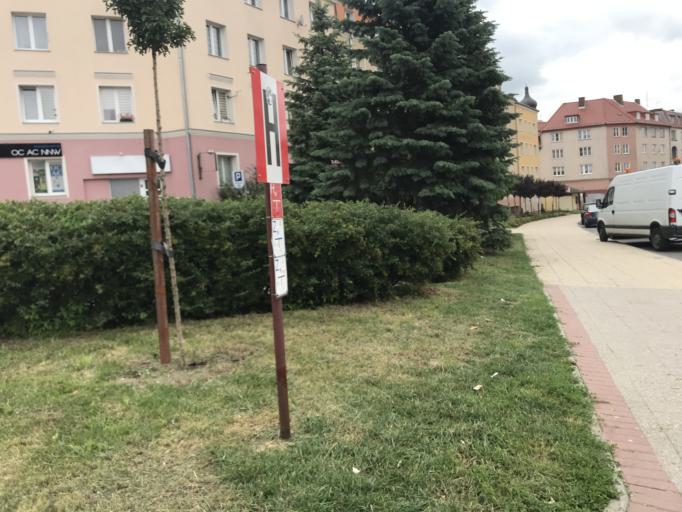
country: PL
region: Warmian-Masurian Voivodeship
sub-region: Powiat elblaski
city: Elblag
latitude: 54.1628
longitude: 19.4057
